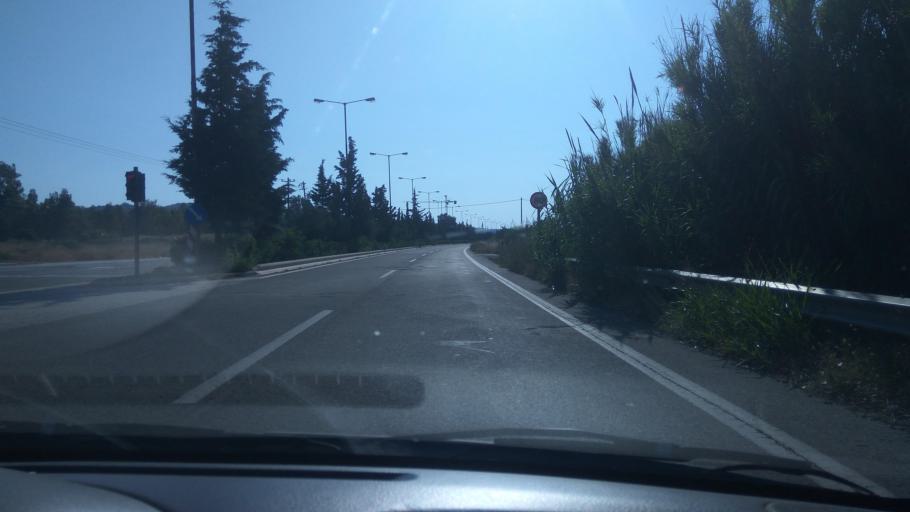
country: GR
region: Attica
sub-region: Nomarchia Anatolikis Attikis
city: Keratea
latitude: 37.8009
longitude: 24.0095
